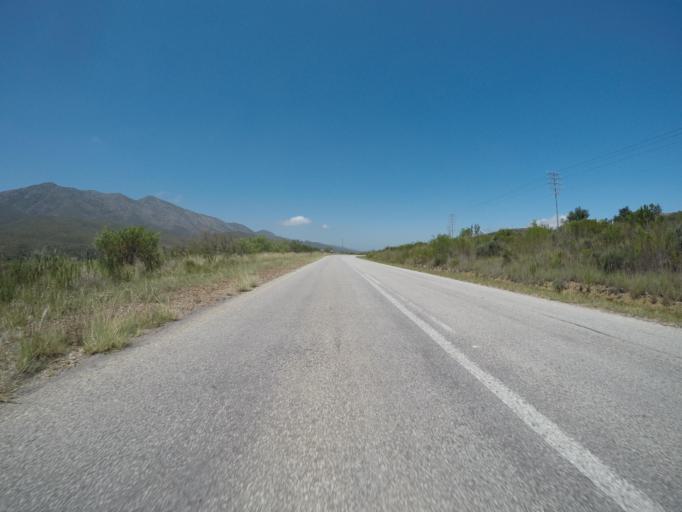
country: ZA
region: Eastern Cape
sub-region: Cacadu District Municipality
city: Kareedouw
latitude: -33.9071
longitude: 24.1555
